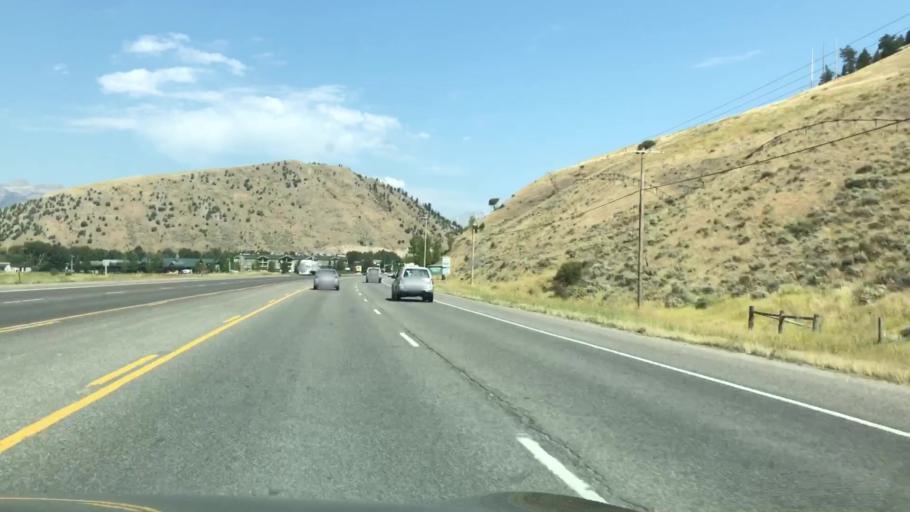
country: US
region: Wyoming
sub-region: Teton County
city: Rafter J Ranch
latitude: 43.4536
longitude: -110.7927
